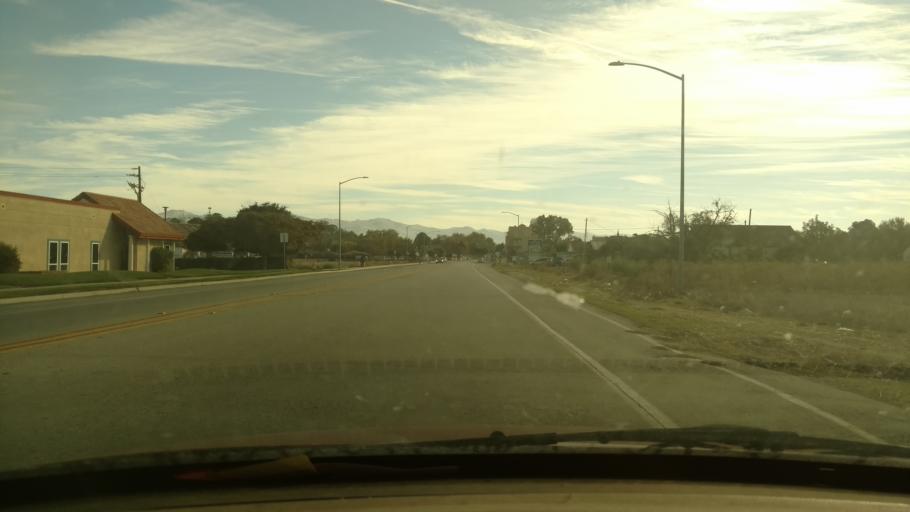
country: US
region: California
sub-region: San Benito County
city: Hollister
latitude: 36.8529
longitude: -121.4168
